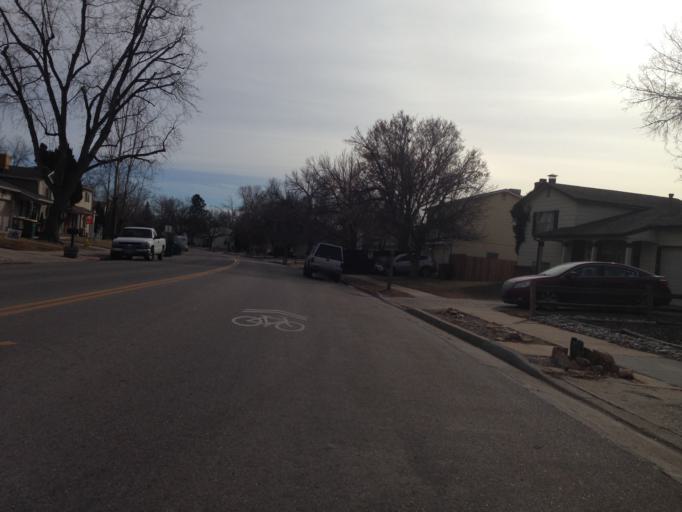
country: US
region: Colorado
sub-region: Adams County
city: Westminster
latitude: 39.8554
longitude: -105.0668
